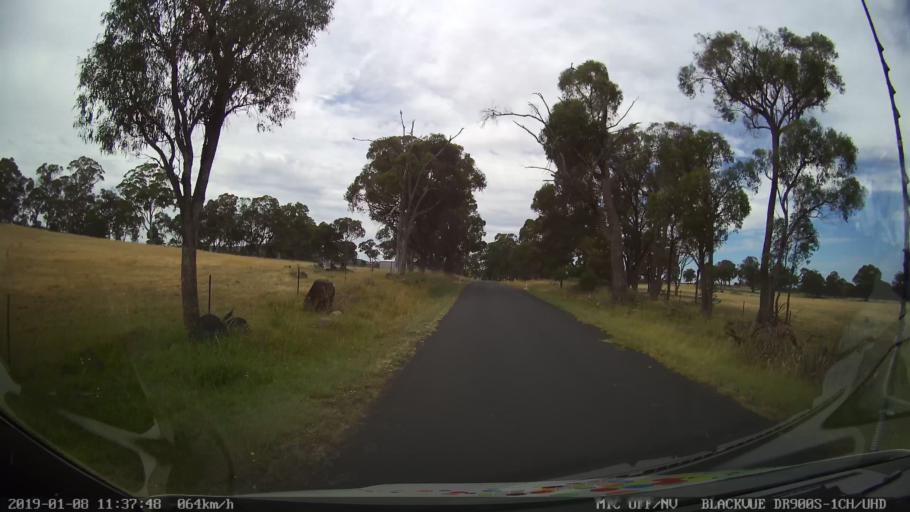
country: AU
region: New South Wales
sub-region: Guyra
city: Guyra
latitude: -30.3549
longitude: 151.5541
